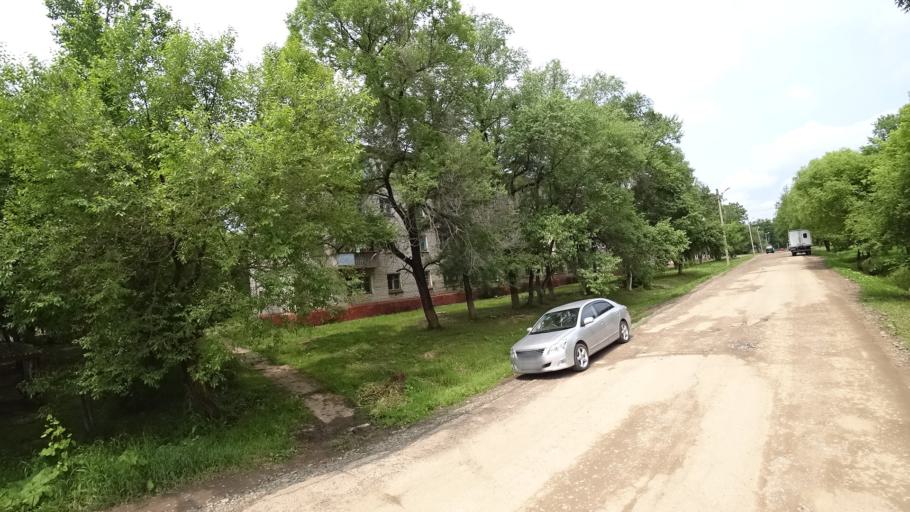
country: RU
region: Primorskiy
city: Novosysoyevka
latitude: 44.2274
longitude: 133.3614
